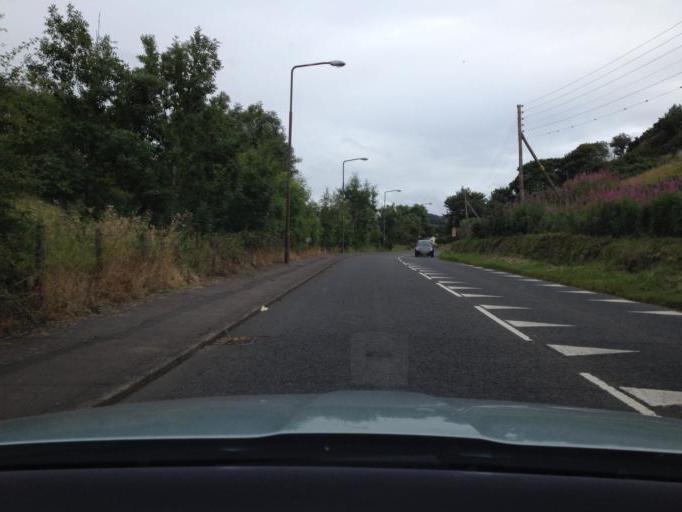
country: GB
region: Scotland
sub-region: West Lothian
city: Bathgate
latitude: 55.9327
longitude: -3.6522
